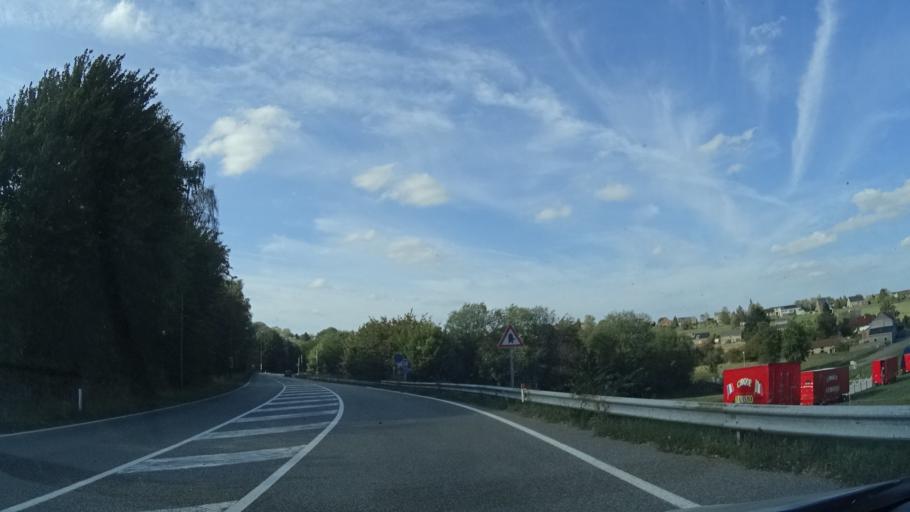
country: BE
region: Wallonia
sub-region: Province de Namur
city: Cerfontaine
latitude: 50.2216
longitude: 4.3831
